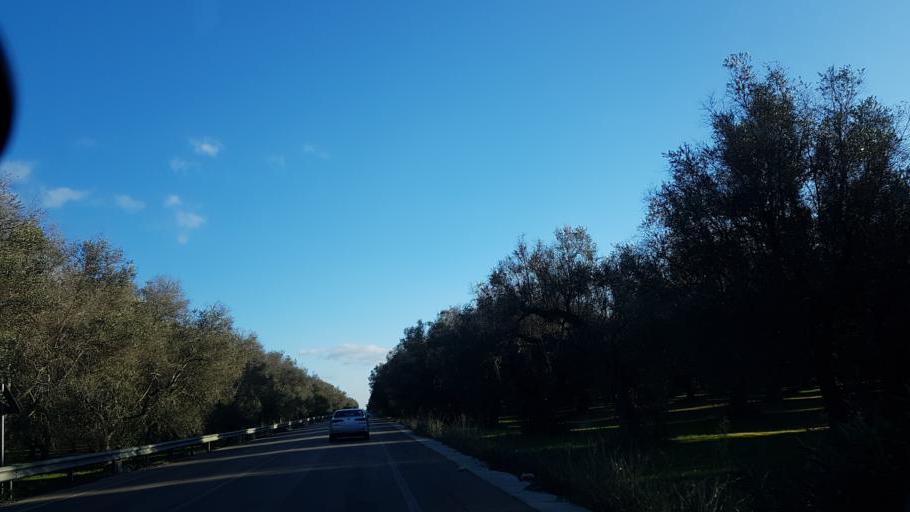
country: IT
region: Apulia
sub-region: Provincia di Brindisi
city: San Pietro Vernotico
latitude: 40.4692
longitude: 18.0139
